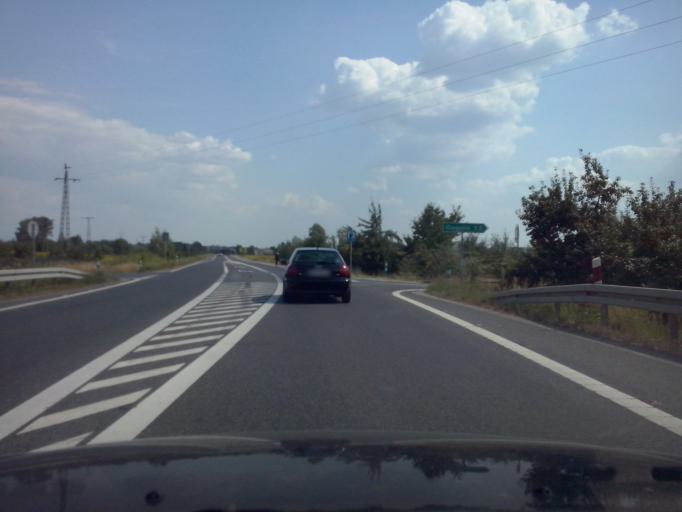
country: PL
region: Subcarpathian Voivodeship
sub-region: Powiat tarnobrzeski
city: Baranow Sandomierski
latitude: 50.5301
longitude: 21.5771
